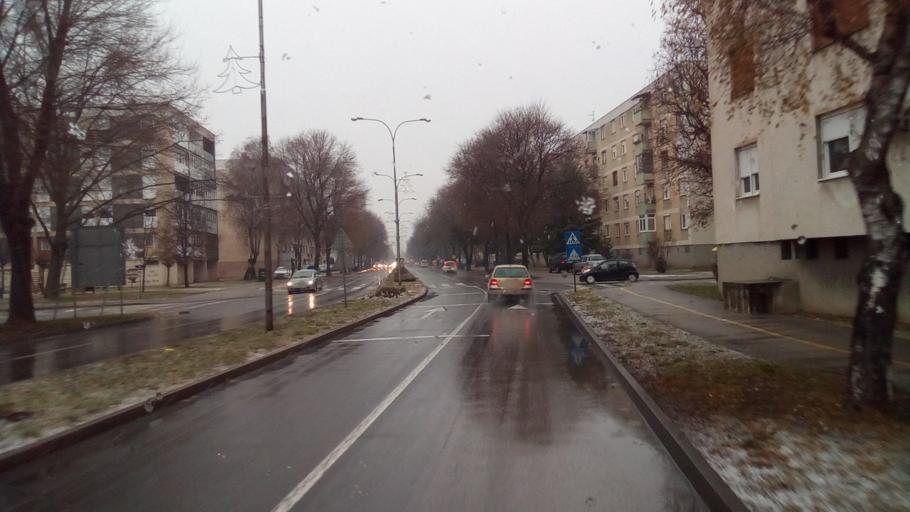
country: HR
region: Varazdinska
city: Varazdin
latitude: 46.2987
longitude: 16.3369
